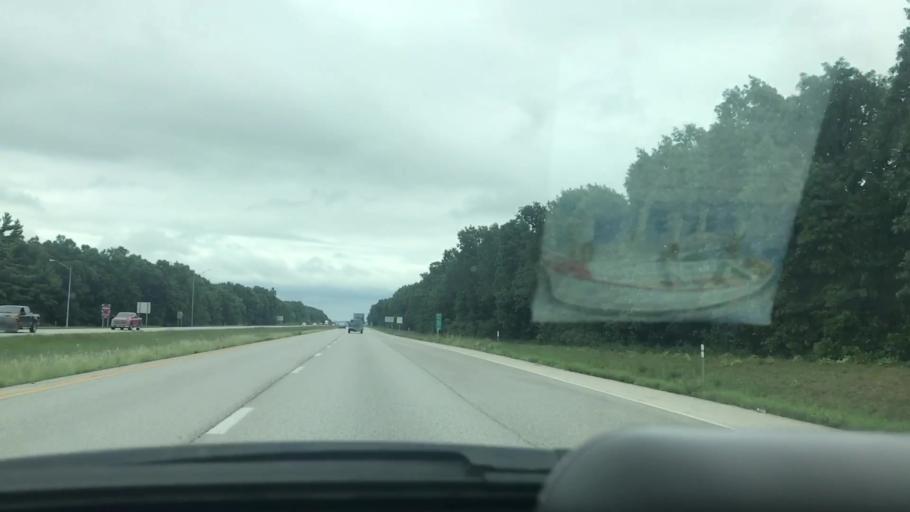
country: US
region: Missouri
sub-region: Lawrence County
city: Mount Vernon
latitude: 37.1403
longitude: -93.7205
